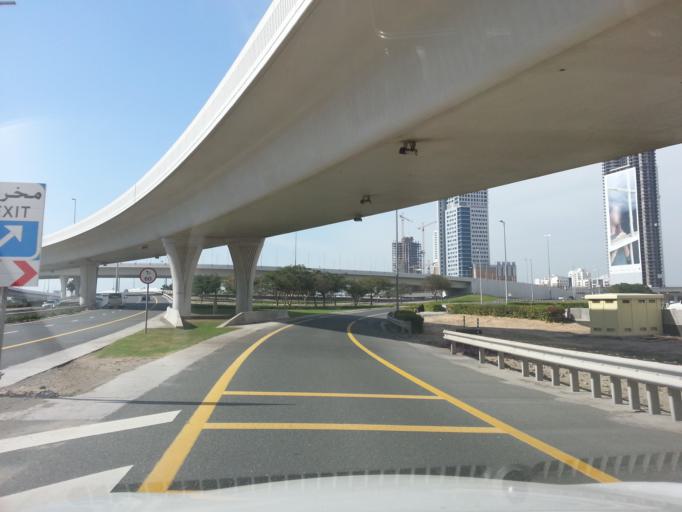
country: AE
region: Dubai
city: Dubai
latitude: 25.1029
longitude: 55.1792
